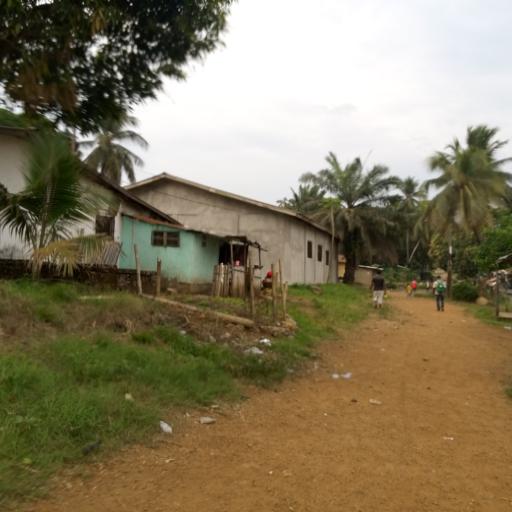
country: LR
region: Montserrado
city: Monrovia
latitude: 6.2999
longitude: -10.6860
